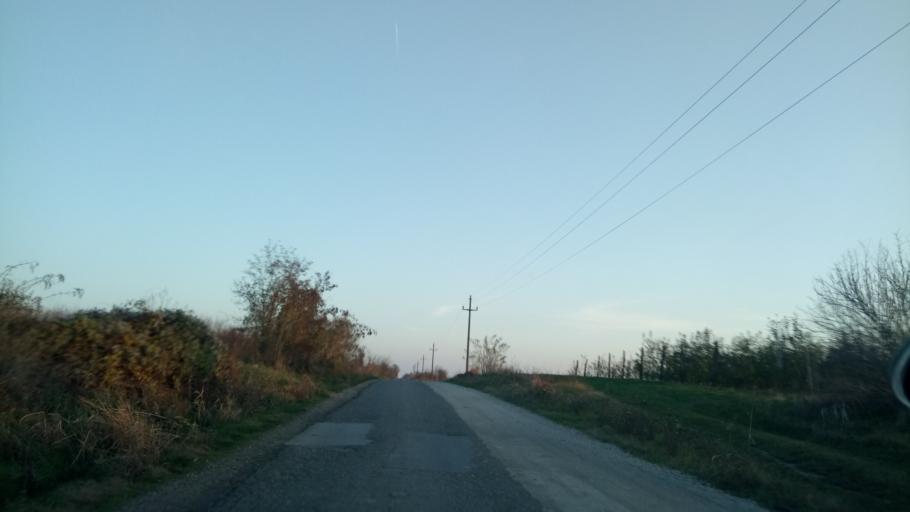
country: RS
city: Novi Slankamen
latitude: 45.1255
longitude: 20.2613
